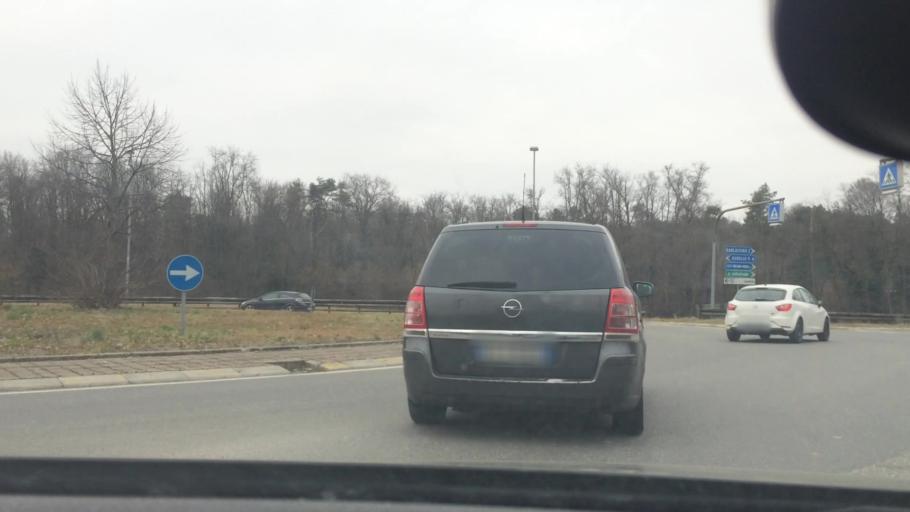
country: IT
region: Lombardy
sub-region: Provincia di Monza e Brianza
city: Cogliate
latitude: 45.6444
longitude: 9.1020
